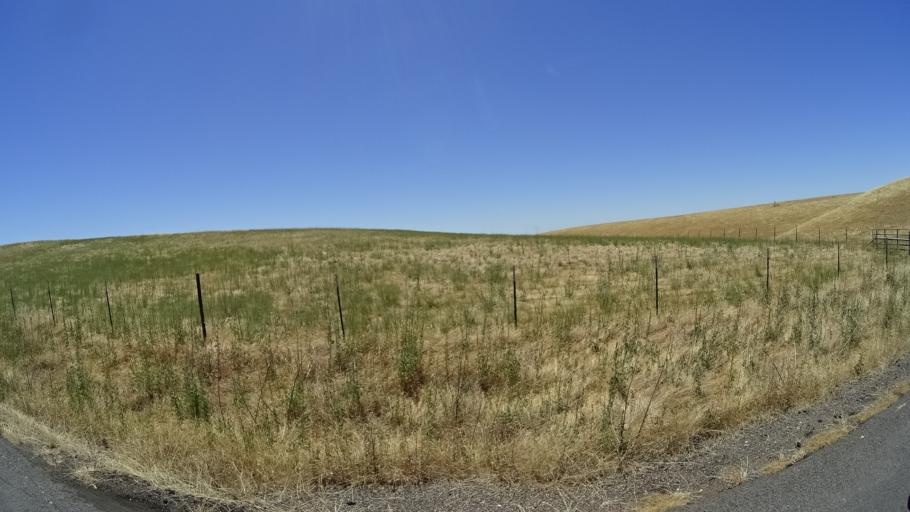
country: US
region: California
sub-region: Calaveras County
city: Rancho Calaveras
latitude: 38.0462
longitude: -120.8317
